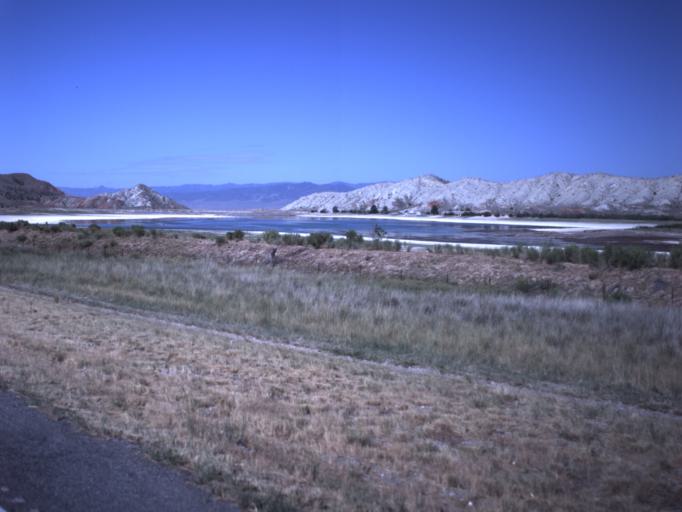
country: US
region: Utah
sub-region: Sanpete County
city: Manti
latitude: 39.1777
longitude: -111.7006
